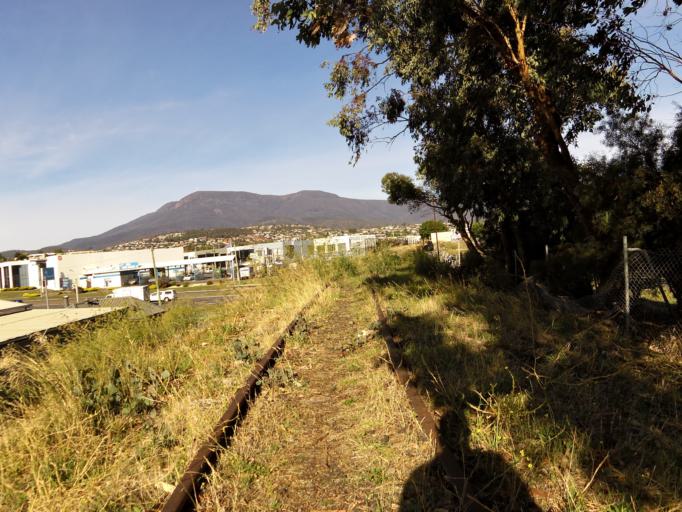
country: AU
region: Tasmania
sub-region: Glenorchy
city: Lutana
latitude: -42.8366
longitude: 147.3031
